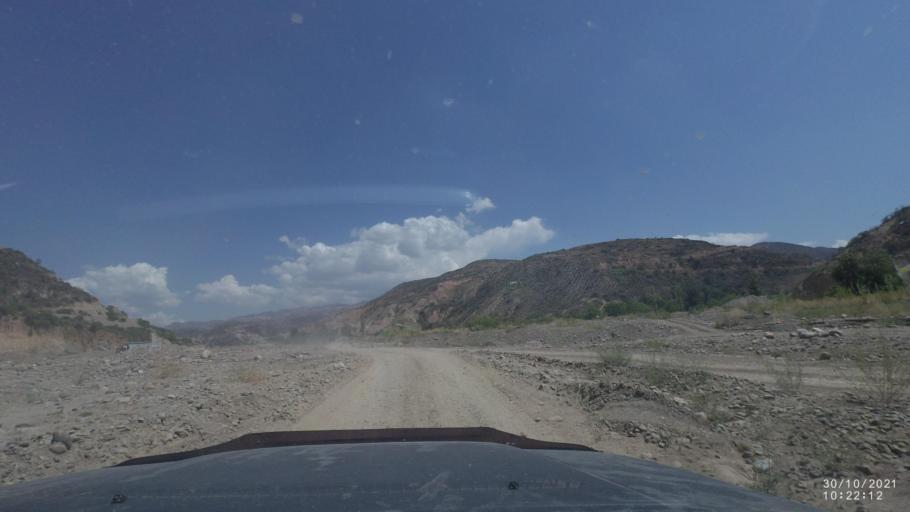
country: BO
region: Cochabamba
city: Sipe Sipe
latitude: -17.5606
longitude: -66.3817
